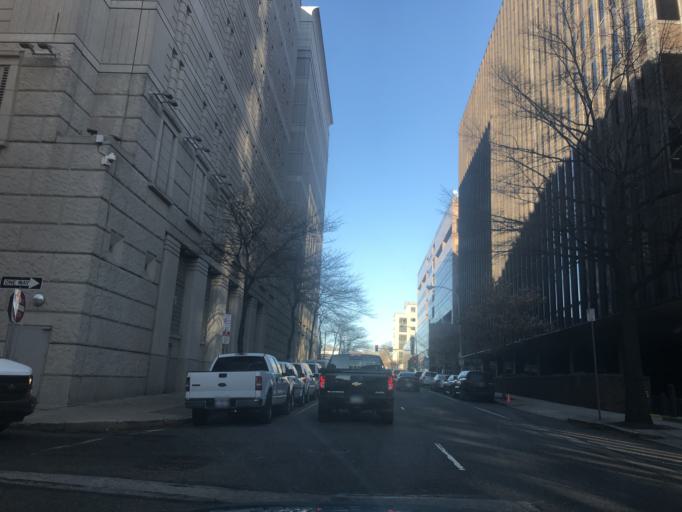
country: US
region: Pennsylvania
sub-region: Philadelphia County
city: Philadelphia
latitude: 39.9519
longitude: -75.1518
